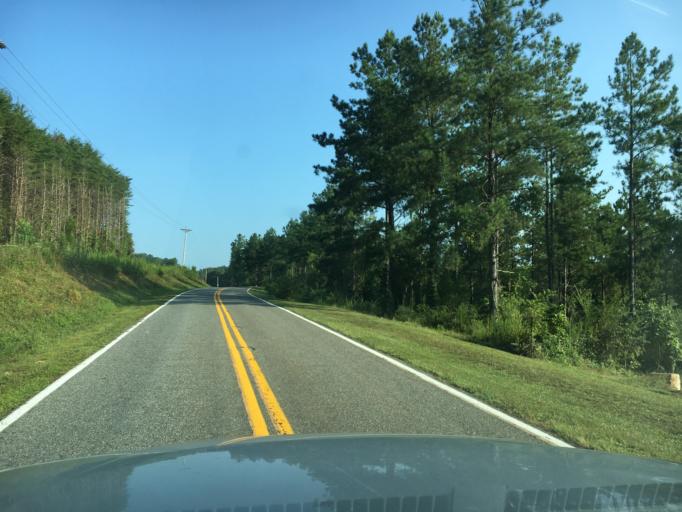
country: US
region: North Carolina
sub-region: Rutherford County
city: Rutherfordton
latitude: 35.2651
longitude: -82.0306
